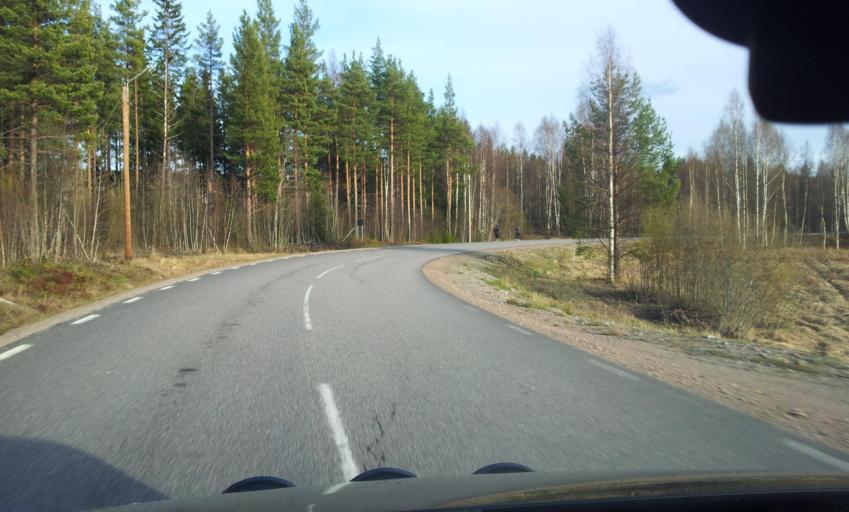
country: SE
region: Vaesternorrland
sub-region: Ange Kommun
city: Ange
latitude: 62.1662
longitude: 15.6774
